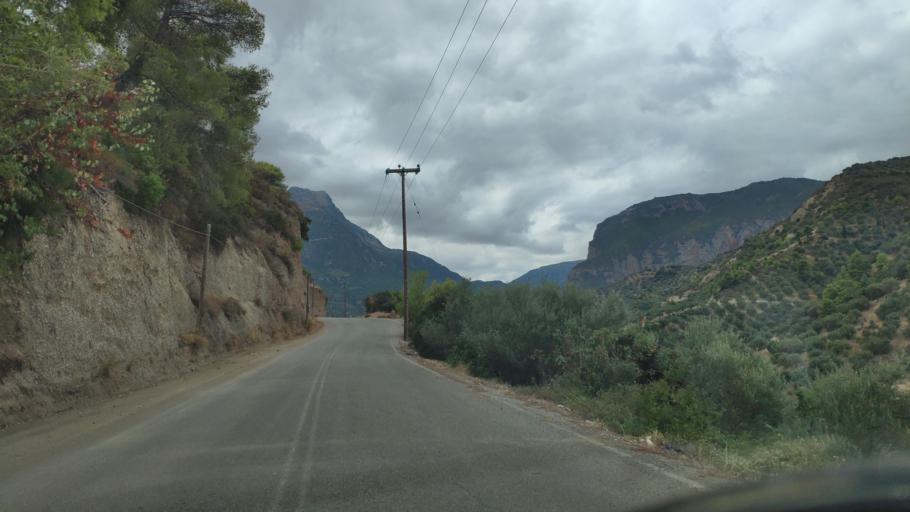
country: GR
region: West Greece
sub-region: Nomos Achaias
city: Temeni
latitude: 38.1873
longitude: 22.1494
